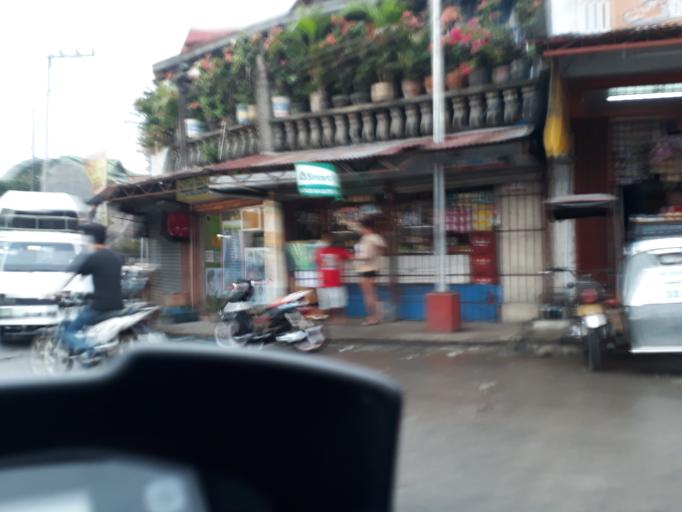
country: PH
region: Central Luzon
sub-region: Province of Bulacan
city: San Jose del Monte
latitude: 14.7733
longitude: 121.0502
